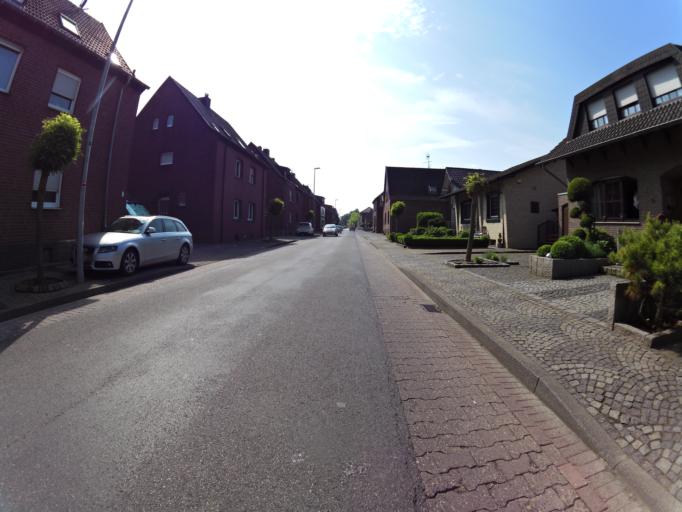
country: DE
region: North Rhine-Westphalia
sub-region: Regierungsbezirk Koln
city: Gangelt
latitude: 51.0079
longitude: 6.0573
